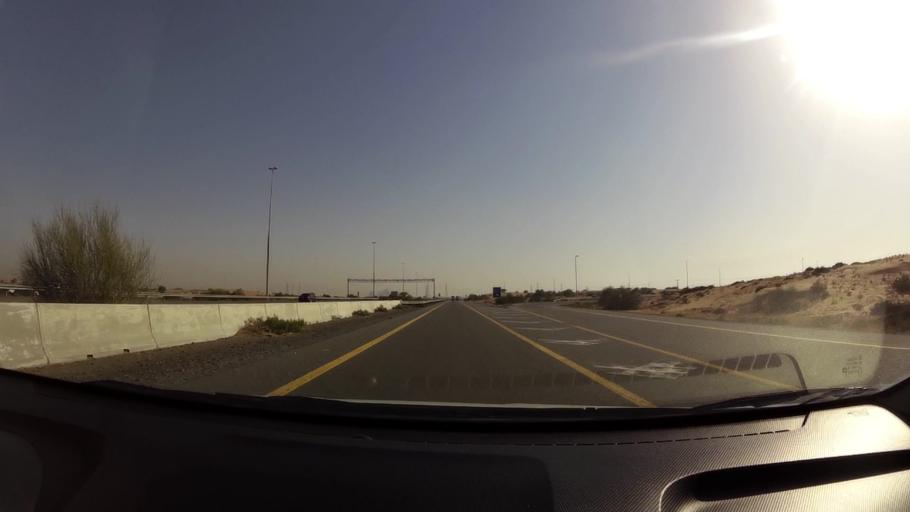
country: AE
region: Umm al Qaywayn
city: Umm al Qaywayn
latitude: 25.4506
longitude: 55.6131
